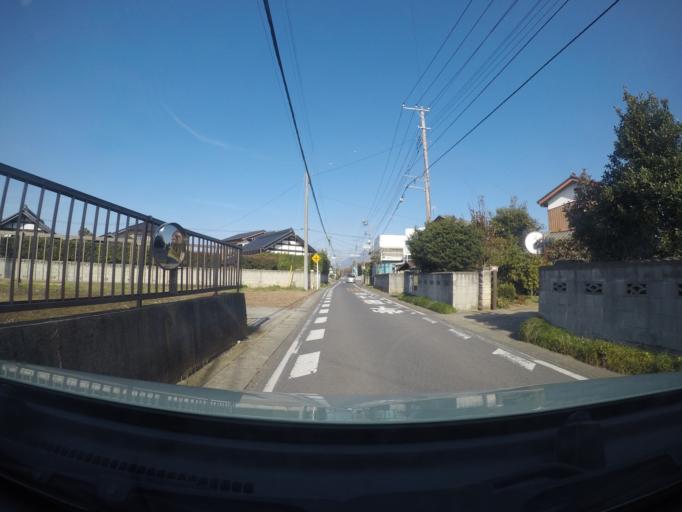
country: JP
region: Ibaraki
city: Tsukuba
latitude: 36.1424
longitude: 140.0875
